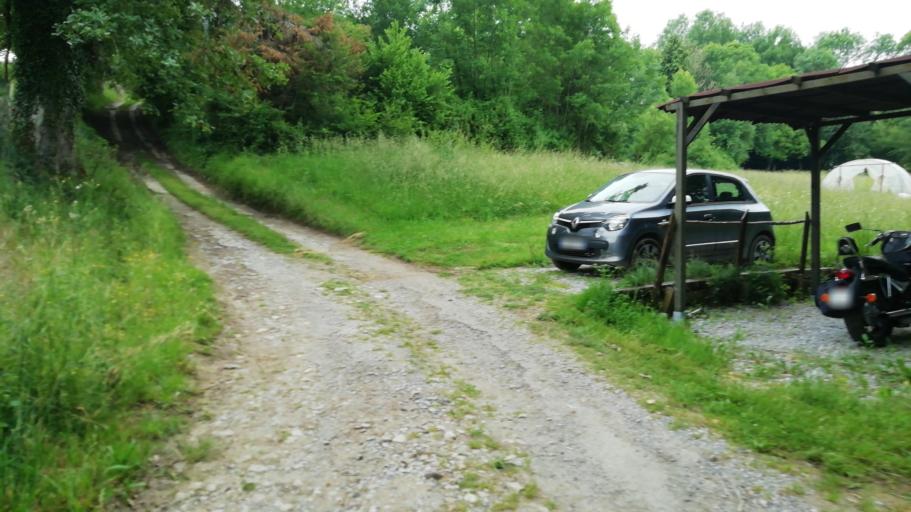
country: FR
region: Aquitaine
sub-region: Departement des Pyrenees-Atlantiques
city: Arudy
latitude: 43.1748
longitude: -0.4262
